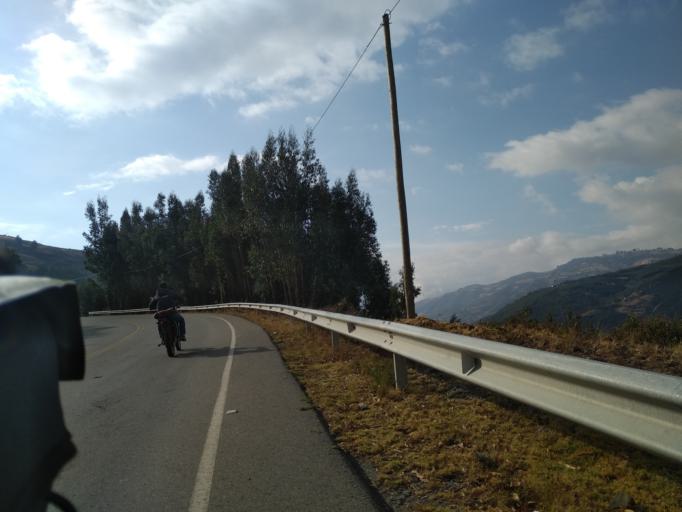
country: PE
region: La Libertad
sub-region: Provincia de Otuzco
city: Agallpampa
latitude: -7.9897
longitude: -78.5306
